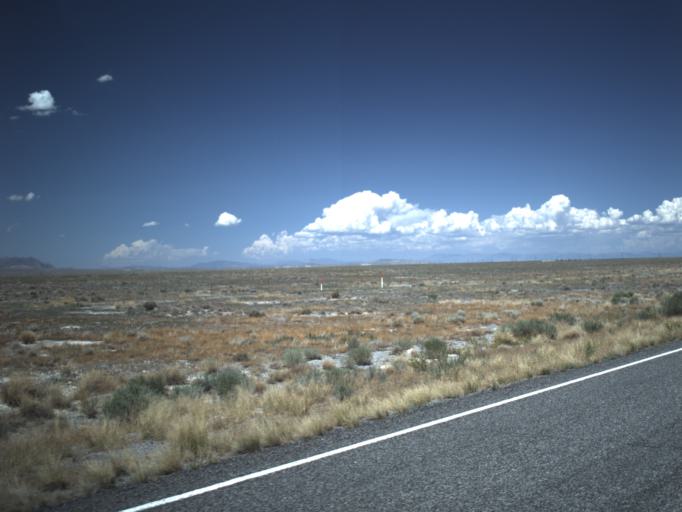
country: US
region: Utah
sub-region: Millard County
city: Delta
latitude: 39.2197
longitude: -112.9500
